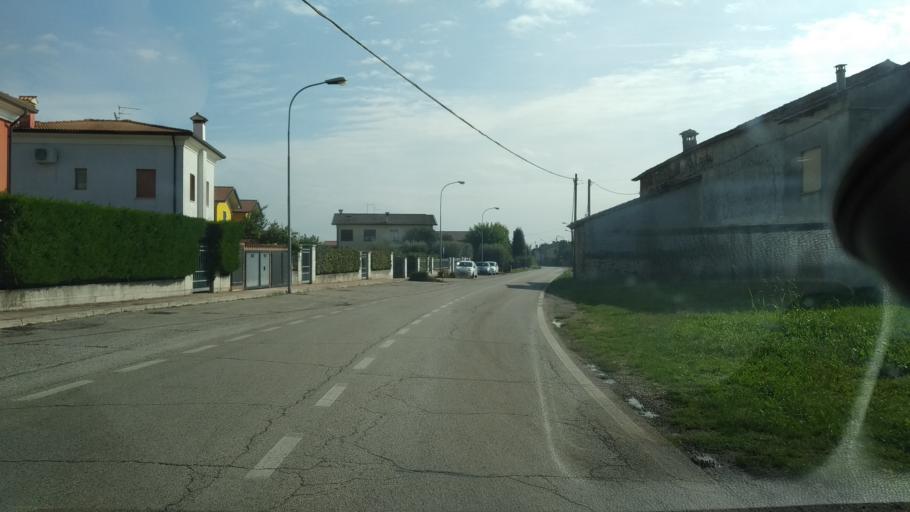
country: IT
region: Veneto
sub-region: Provincia di Vicenza
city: Mason Vicentino
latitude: 45.6960
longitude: 11.5979
